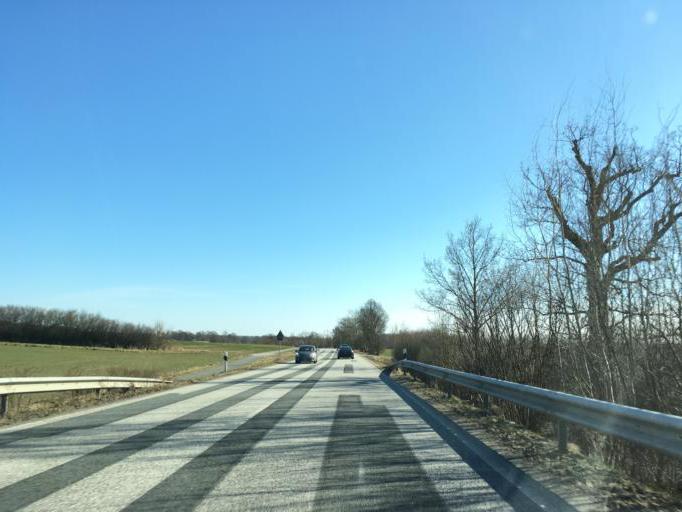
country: DE
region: Schleswig-Holstein
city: Kulpin
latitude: 53.7193
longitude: 10.6814
